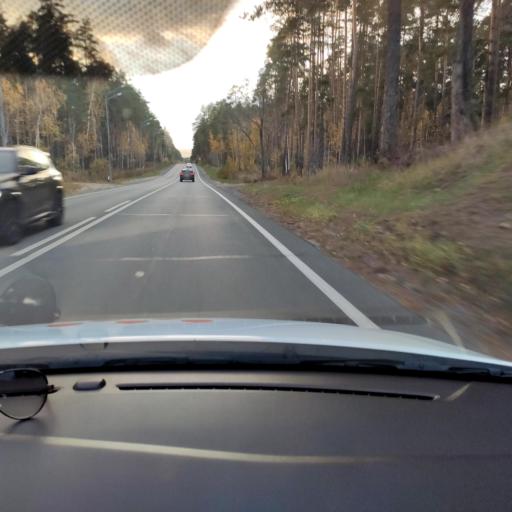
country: RU
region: Tatarstan
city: Verkhniy Uslon
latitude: 55.6380
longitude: 49.0467
